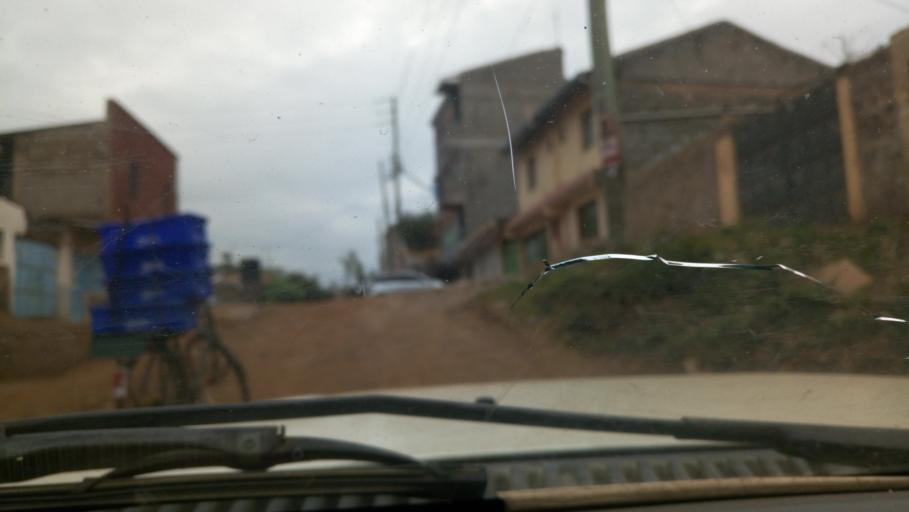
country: KE
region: Kiambu
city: Kiambu
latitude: -1.1837
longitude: 36.8958
